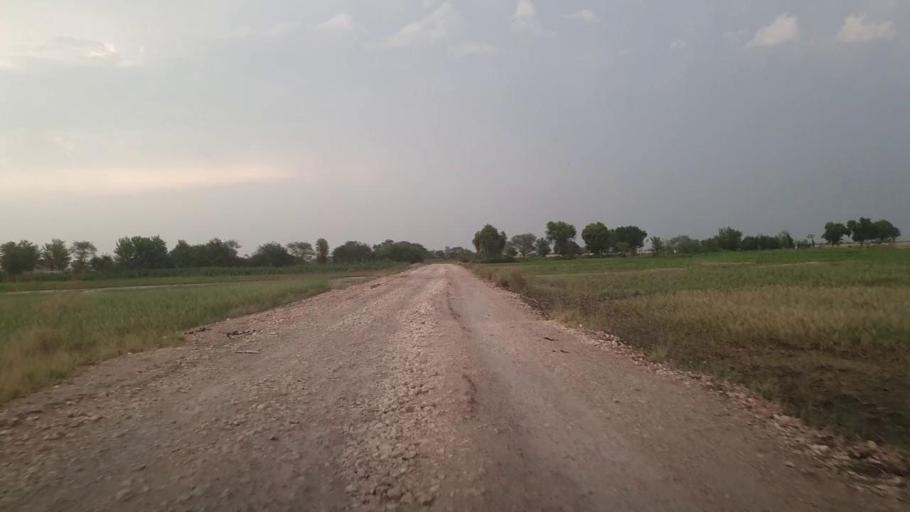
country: PK
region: Sindh
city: Karaundi
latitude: 27.0425
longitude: 68.3780
